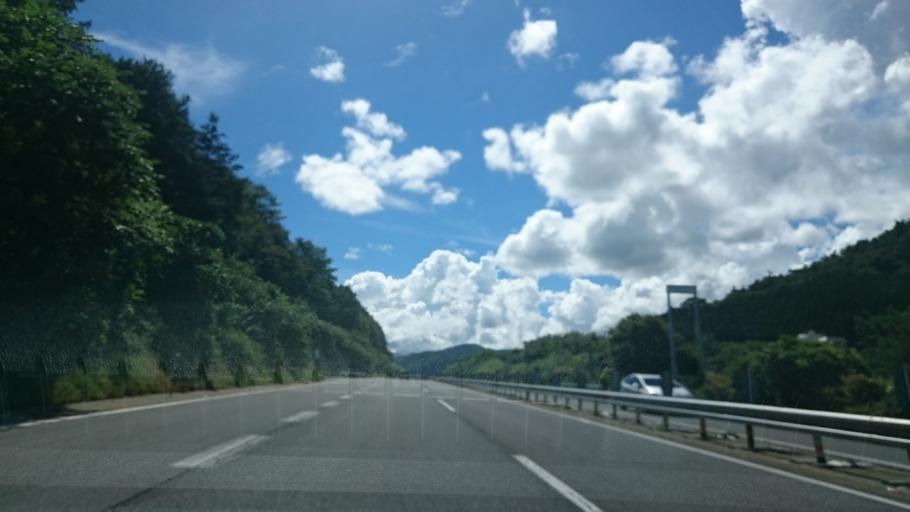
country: JP
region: Nagano
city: Iida
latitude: 35.4853
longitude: 137.7755
